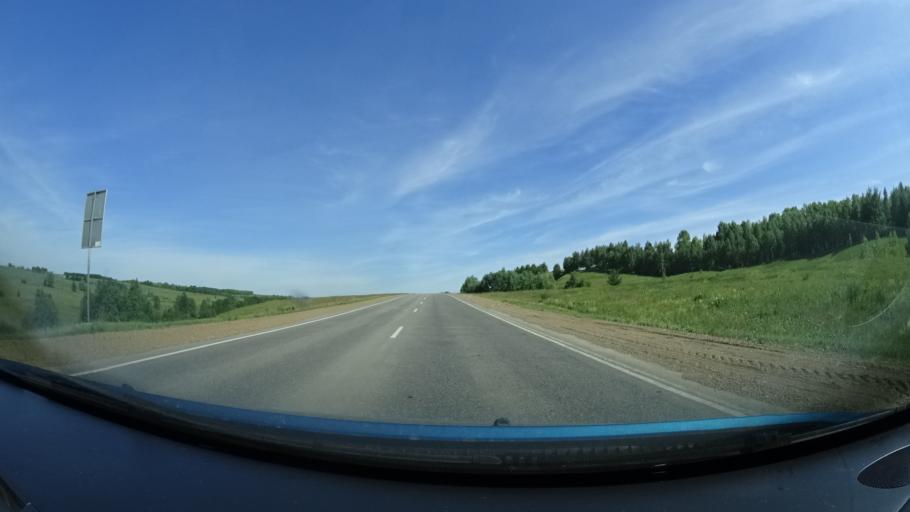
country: RU
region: Bashkortostan
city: Blagoveshchensk
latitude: 55.1147
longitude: 55.8411
